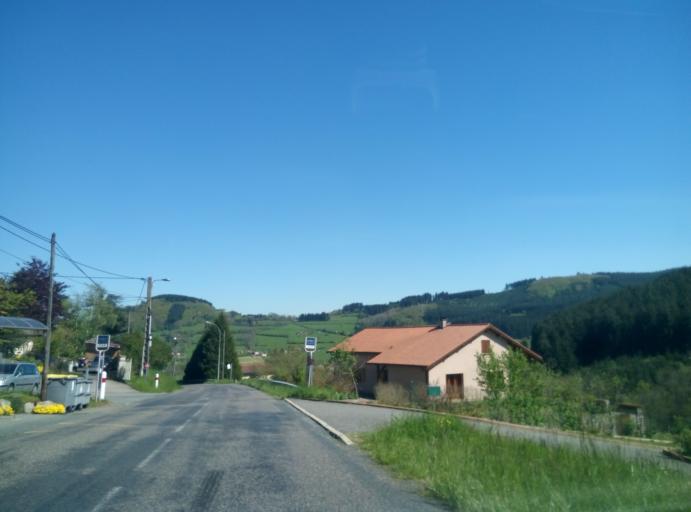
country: FR
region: Rhone-Alpes
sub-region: Departement du Rhone
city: Grandris
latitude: 46.0025
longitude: 4.4398
